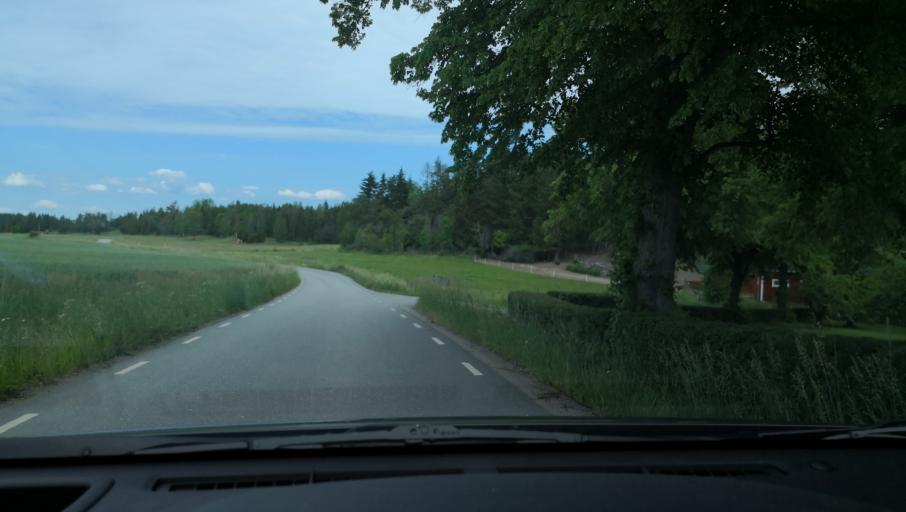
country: SE
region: Uppsala
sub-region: Habo Kommun
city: Balsta
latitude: 59.6963
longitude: 17.4804
